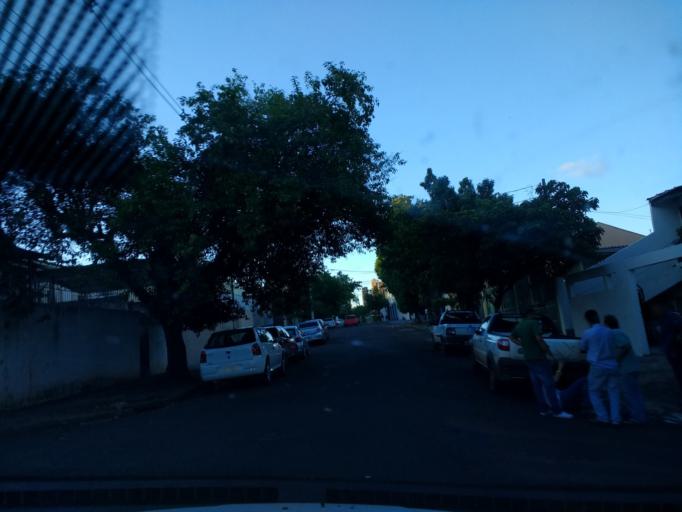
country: BR
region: Parana
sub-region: Londrina
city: Londrina
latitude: -23.3259
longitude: -51.1653
